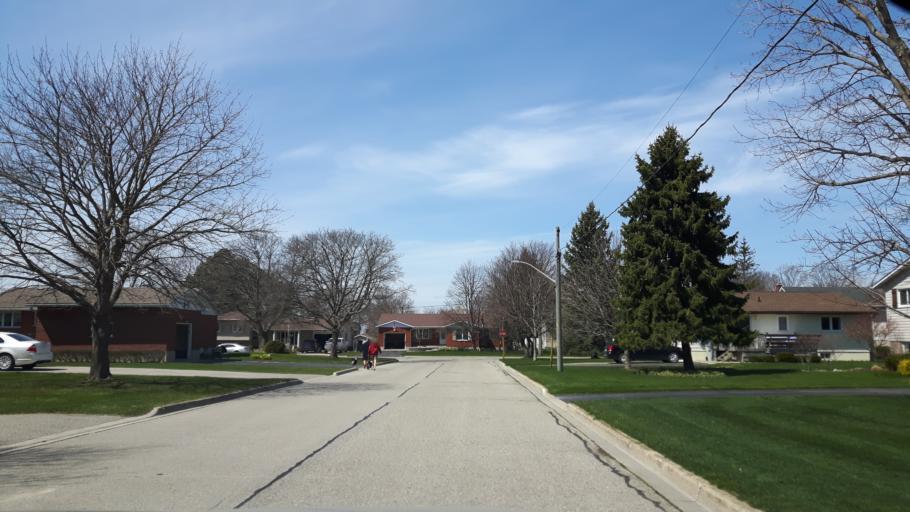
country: CA
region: Ontario
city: Goderich
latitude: 43.7327
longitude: -81.7205
